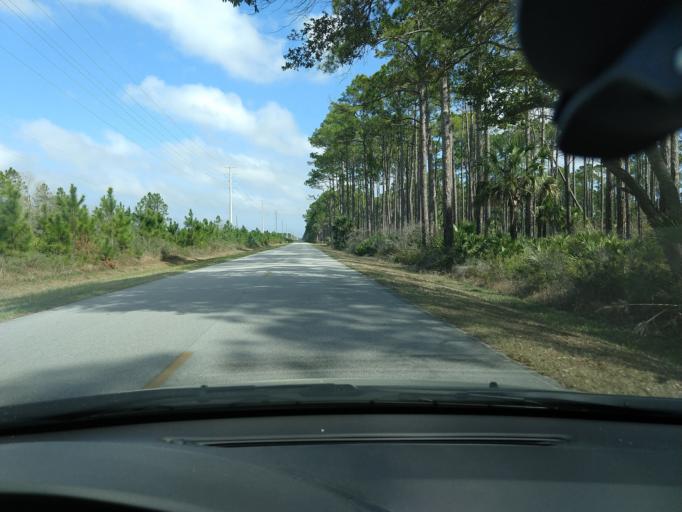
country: US
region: Florida
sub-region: Gulf County
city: Port Saint Joe
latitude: 29.7003
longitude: -85.2046
